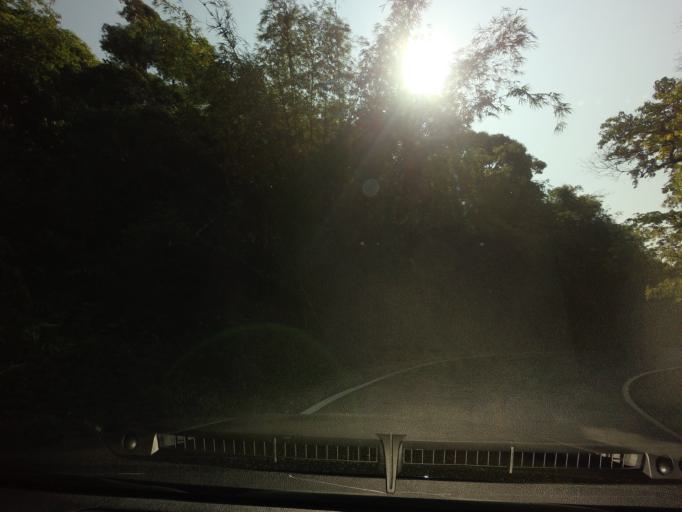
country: TH
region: Kanchanaburi
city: Thong Pha Phum
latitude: 14.6849
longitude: 98.4167
